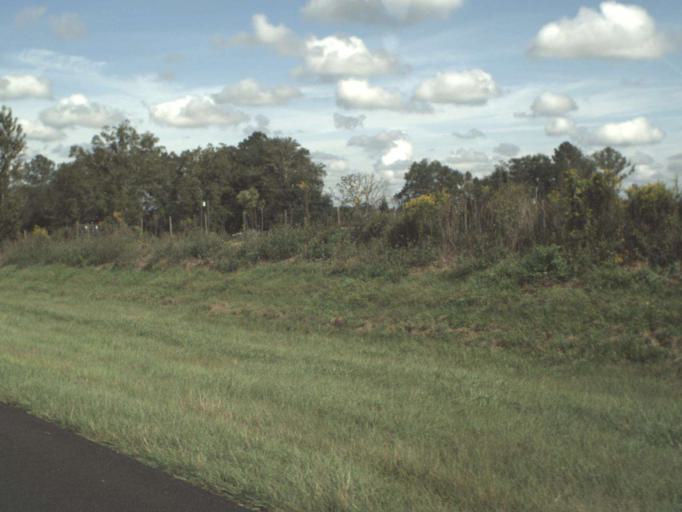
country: US
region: Florida
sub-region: Jackson County
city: Graceville
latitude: 30.9295
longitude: -85.3866
